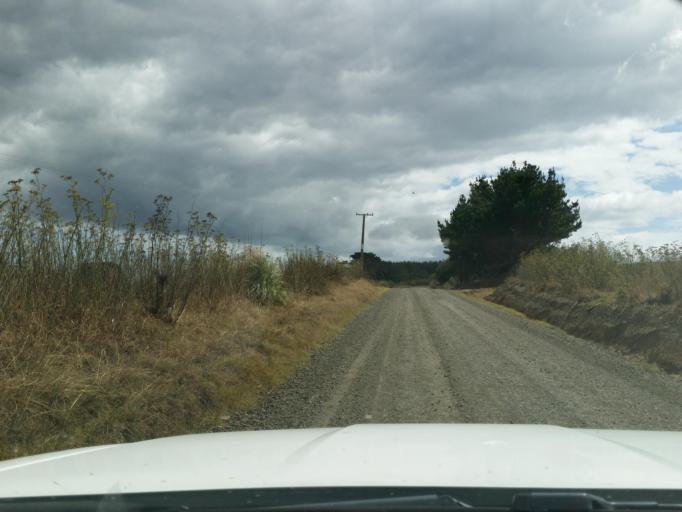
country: NZ
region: Auckland
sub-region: Auckland
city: Wellsford
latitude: -36.3396
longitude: 174.1618
